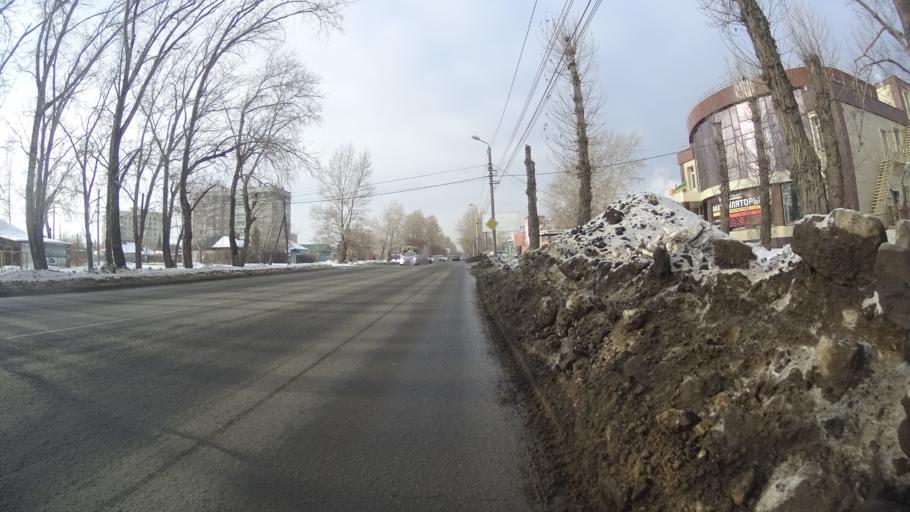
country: RU
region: Chelyabinsk
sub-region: Gorod Chelyabinsk
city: Chelyabinsk
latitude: 55.1220
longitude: 61.3768
